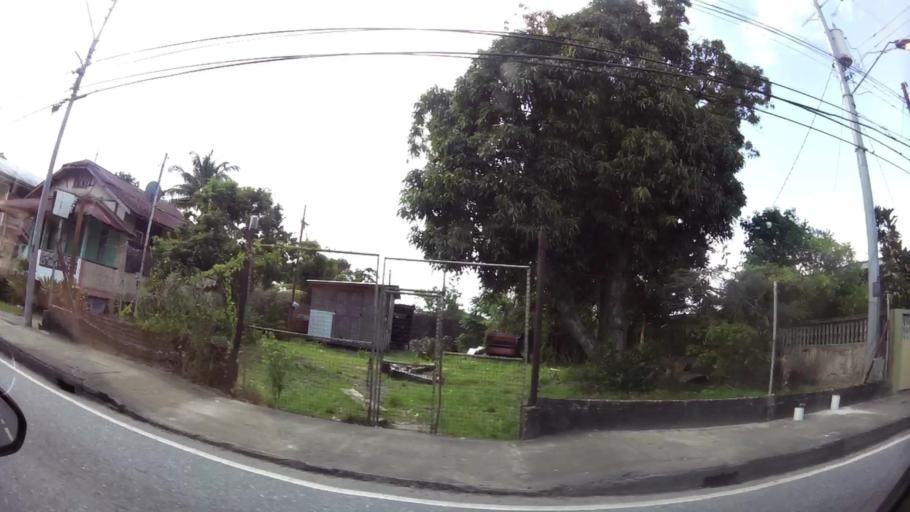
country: TT
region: Borough of Arima
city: Arima
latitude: 10.6337
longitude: -61.2761
